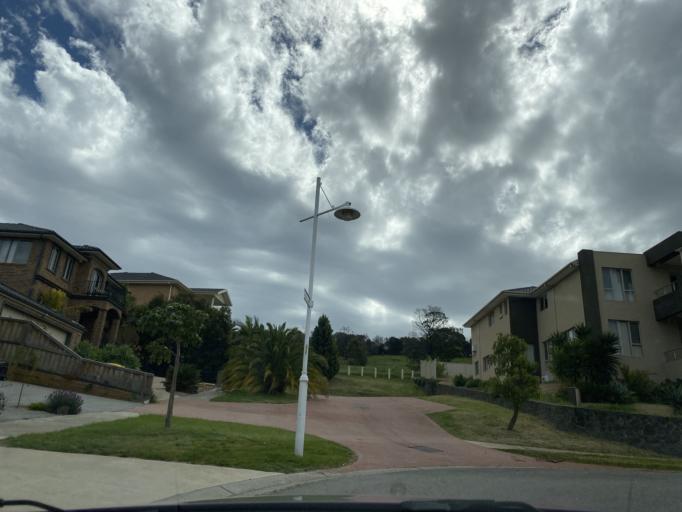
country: AU
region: Victoria
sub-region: Whittlesea
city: Mill Park
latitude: -37.6307
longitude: 145.0641
